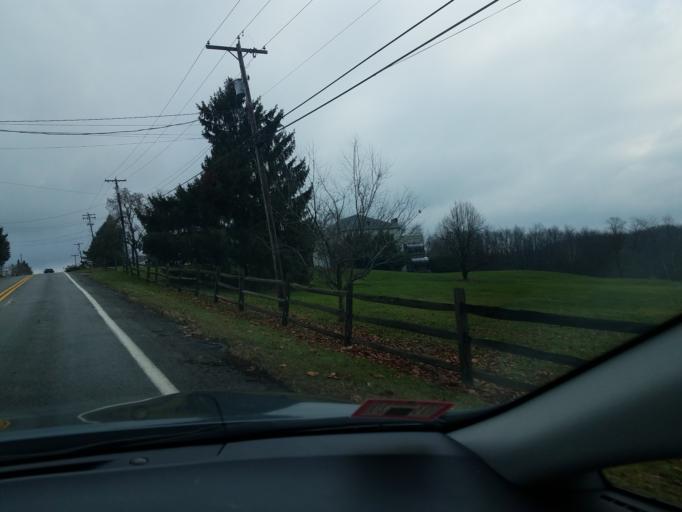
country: US
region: Pennsylvania
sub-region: Allegheny County
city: Franklin Park
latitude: 40.5954
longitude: -80.1000
